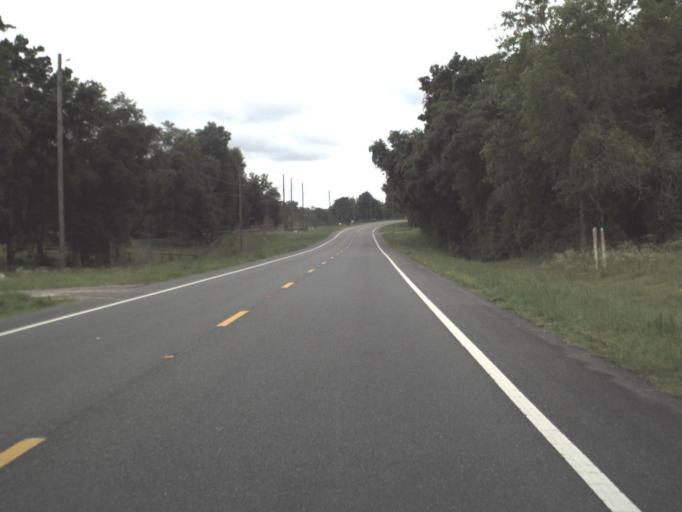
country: US
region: Florida
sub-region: Levy County
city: Williston
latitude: 29.2698
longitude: -82.4424
